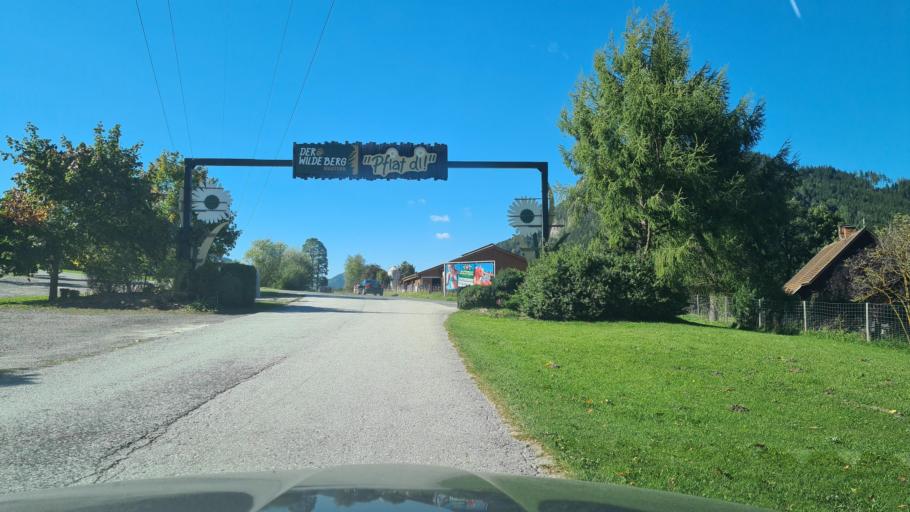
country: AT
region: Styria
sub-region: Politischer Bezirk Leoben
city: Mautern in Steiermark
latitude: 47.3945
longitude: 14.8169
